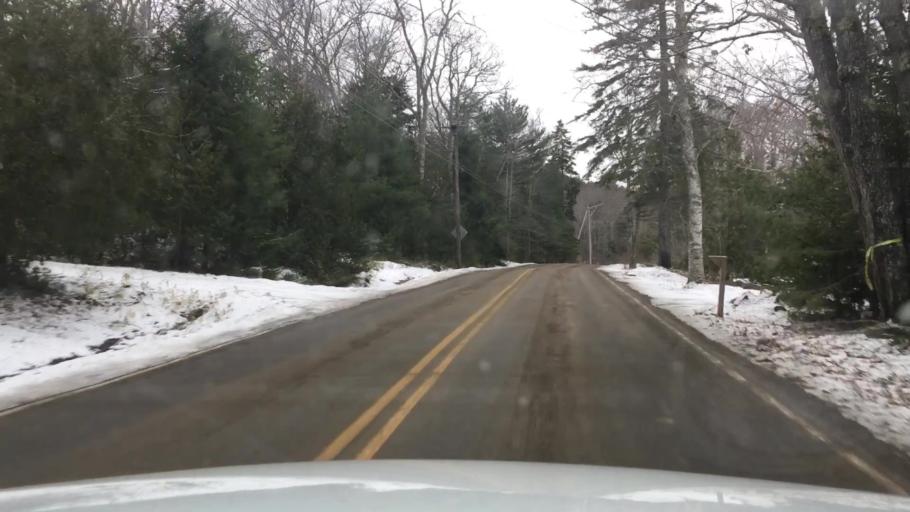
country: US
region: Maine
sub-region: Waldo County
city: Lincolnville
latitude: 44.2829
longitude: -69.0129
